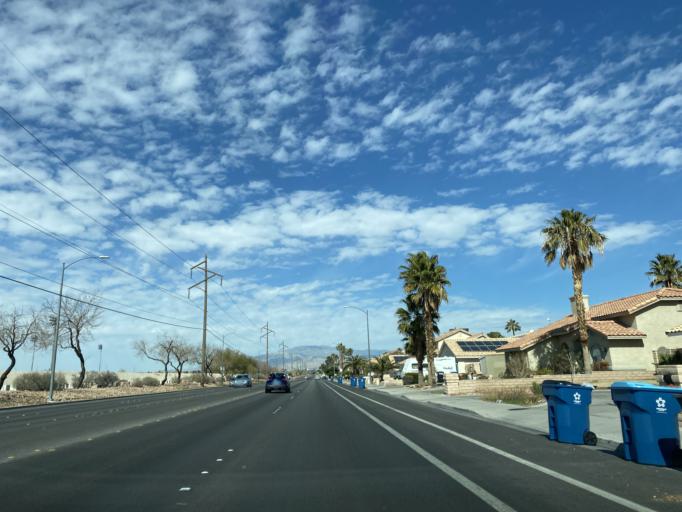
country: US
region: Nevada
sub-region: Clark County
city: Spring Valley
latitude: 36.2222
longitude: -115.2513
